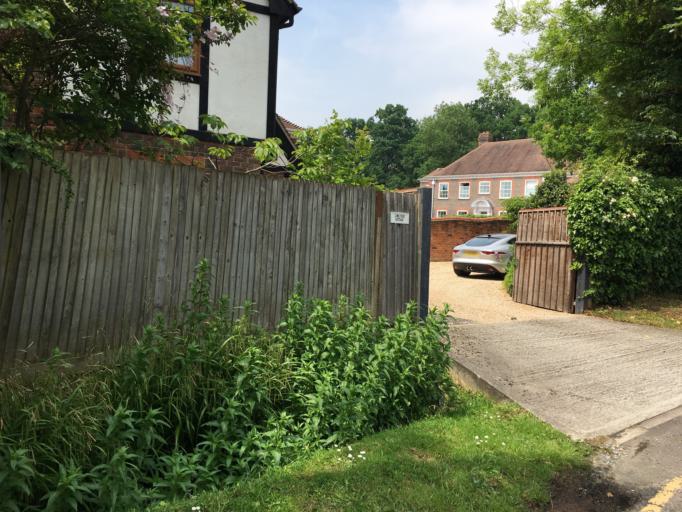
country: GB
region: England
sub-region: West Berkshire
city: Tilehurst
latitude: 51.4455
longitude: -1.0263
